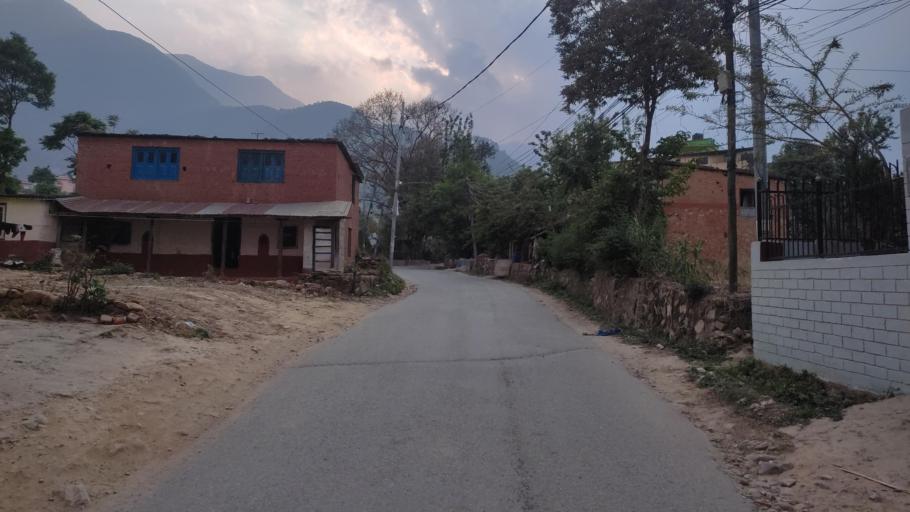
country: NP
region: Central Region
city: Kirtipur
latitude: 27.6668
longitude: 85.2590
